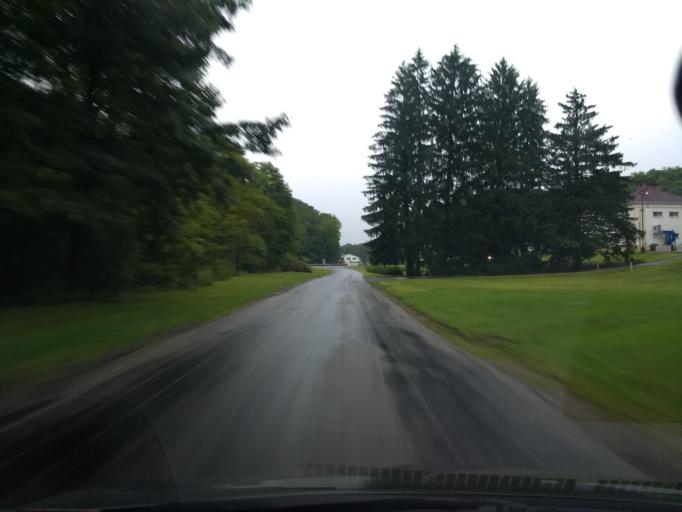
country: US
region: Pennsylvania
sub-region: Westmoreland County
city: Greensburg
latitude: 40.3555
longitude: -79.5228
